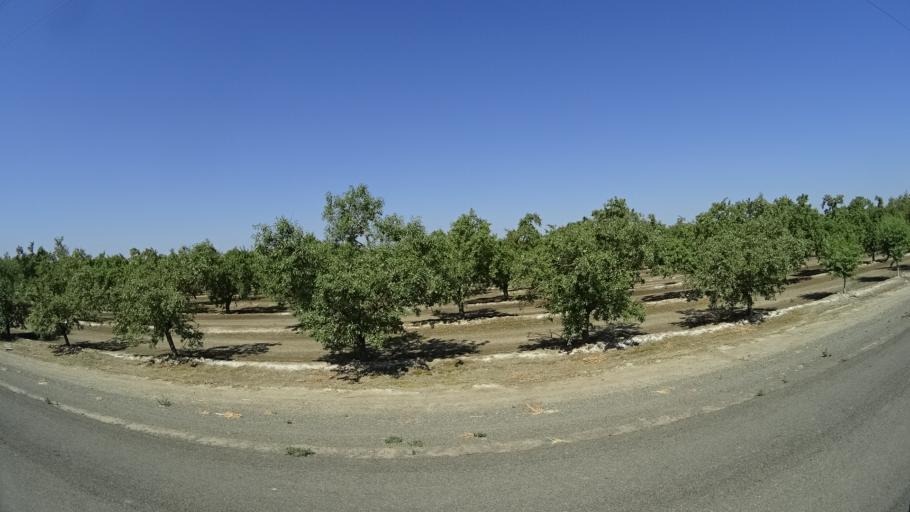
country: US
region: California
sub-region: Kings County
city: Lucerne
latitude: 36.3806
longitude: -119.5830
